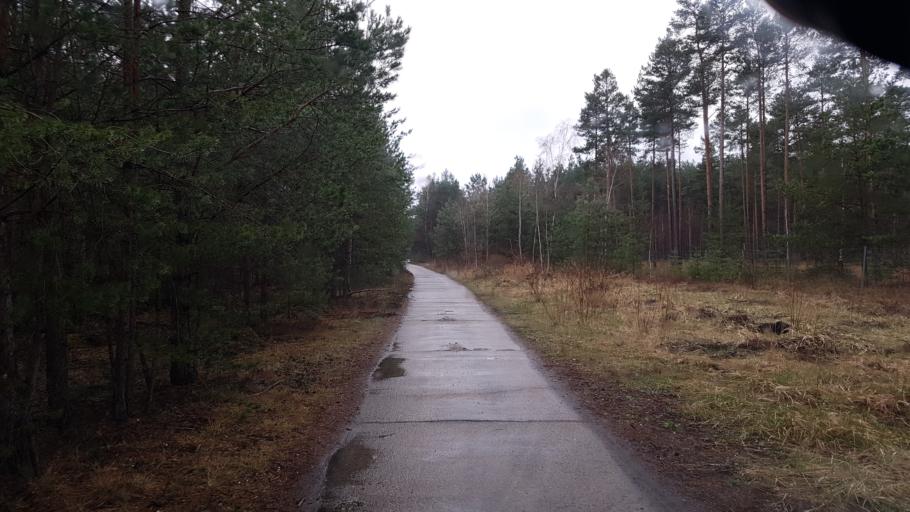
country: DE
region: Brandenburg
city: Grossraschen
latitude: 51.5996
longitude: 13.9919
